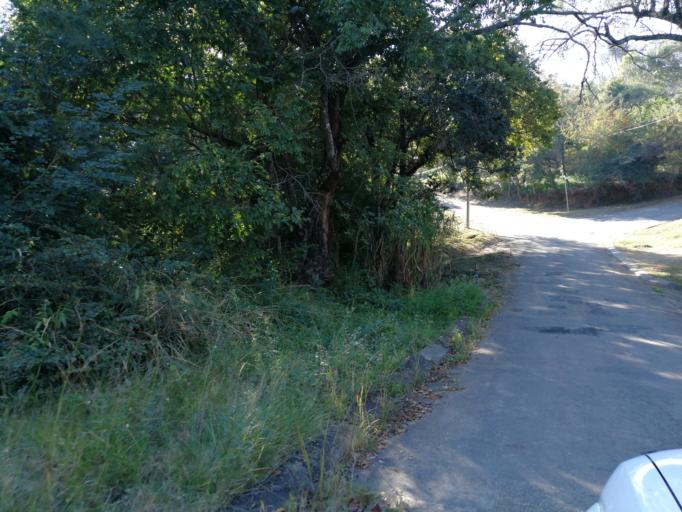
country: ZA
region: Mpumalanga
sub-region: Ehlanzeni District
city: White River
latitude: -25.0661
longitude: 31.1134
